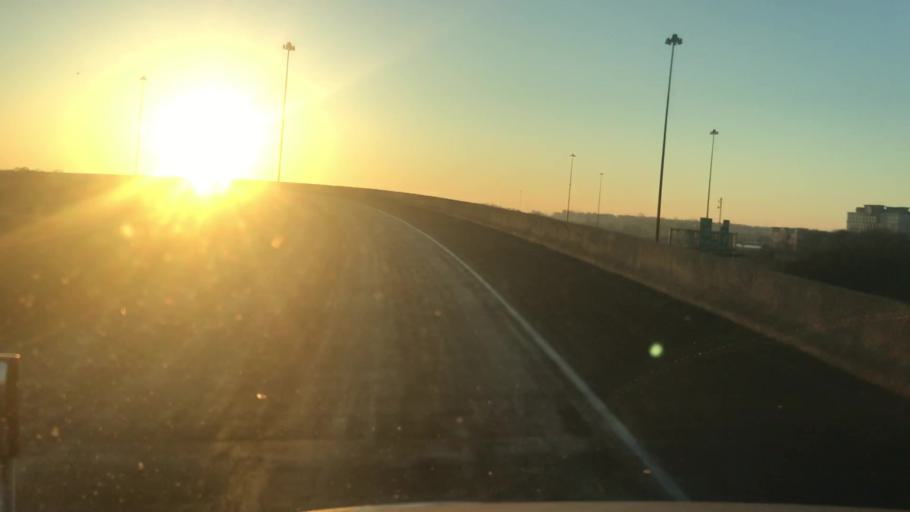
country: US
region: Iowa
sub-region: Black Hawk County
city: Evansdale
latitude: 42.4547
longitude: -92.3132
